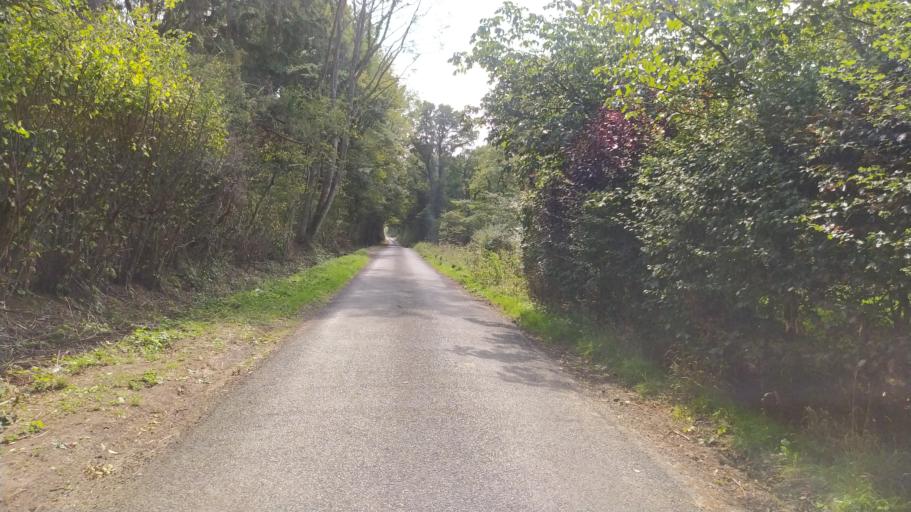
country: GB
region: England
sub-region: Surrey
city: Farnham
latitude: 51.2006
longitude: -0.8505
